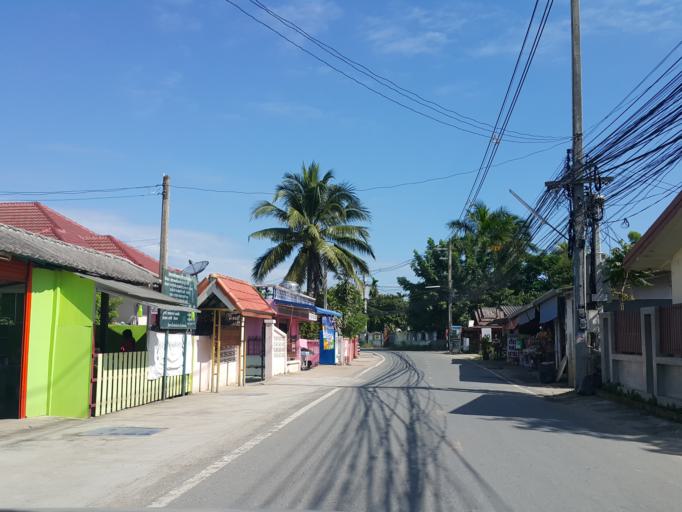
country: TH
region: Chiang Mai
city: San Sai
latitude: 18.7939
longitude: 99.0458
